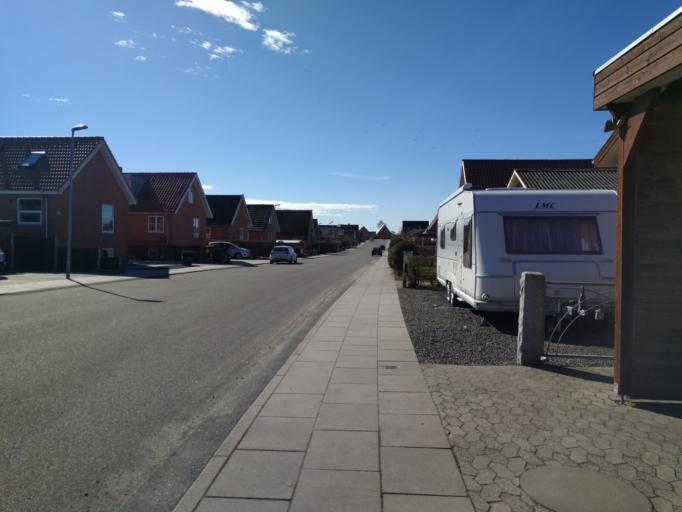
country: DK
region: Central Jutland
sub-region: Viborg Kommune
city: Viborg
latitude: 56.4621
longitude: 9.3871
